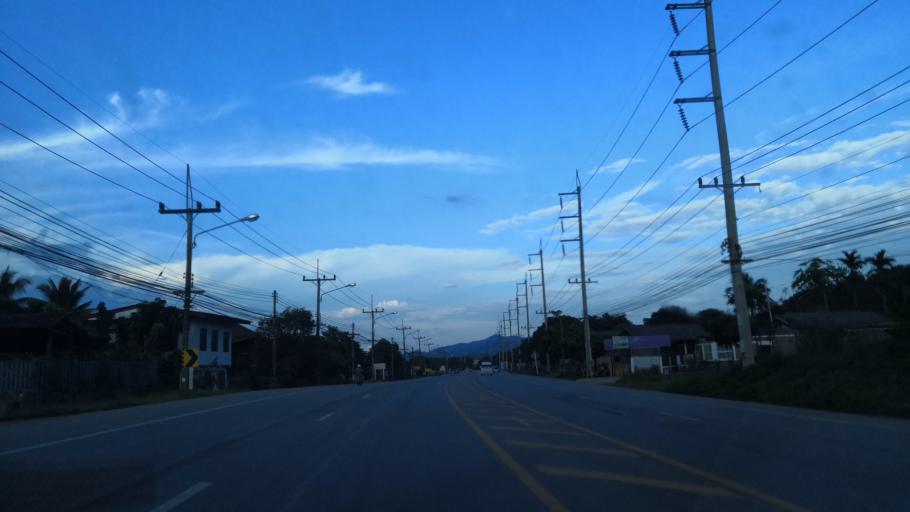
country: TH
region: Chiang Rai
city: Mae Suai
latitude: 19.6391
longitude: 99.5201
